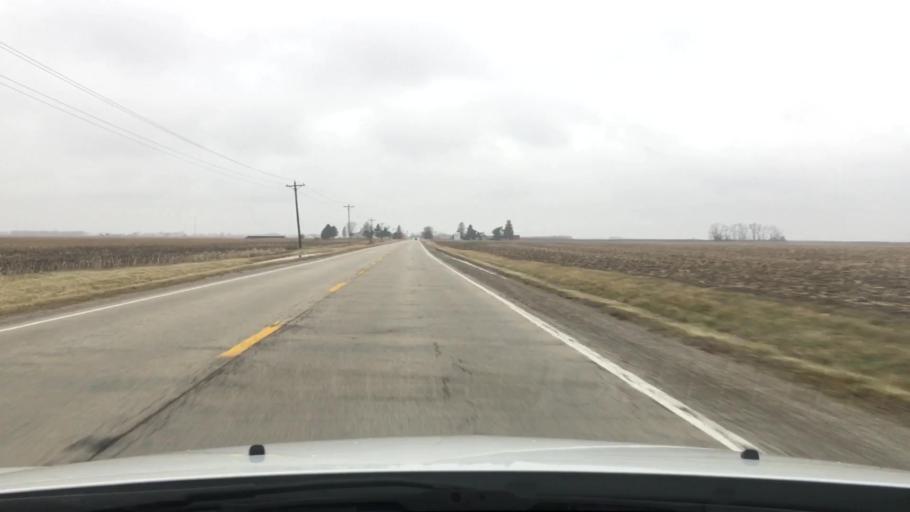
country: US
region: Illinois
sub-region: Iroquois County
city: Watseka
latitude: 40.8905
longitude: -87.6961
